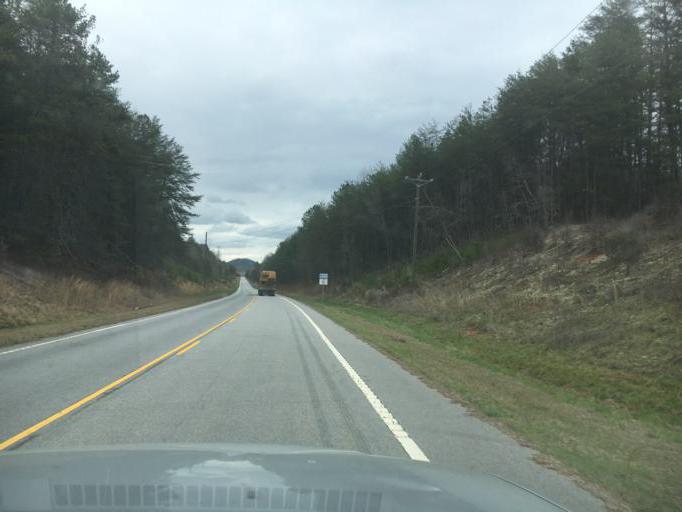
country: US
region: South Carolina
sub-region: Pickens County
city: Pickens
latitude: 34.9633
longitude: -82.8243
